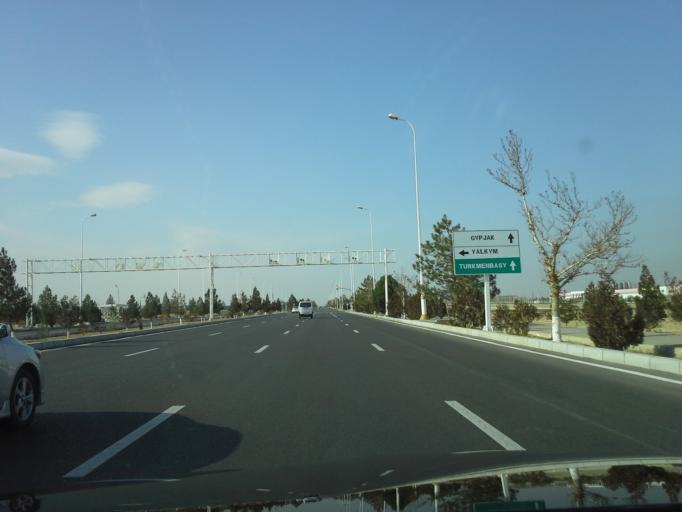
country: TM
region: Ahal
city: Ashgabat
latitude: 37.9997
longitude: 58.3012
